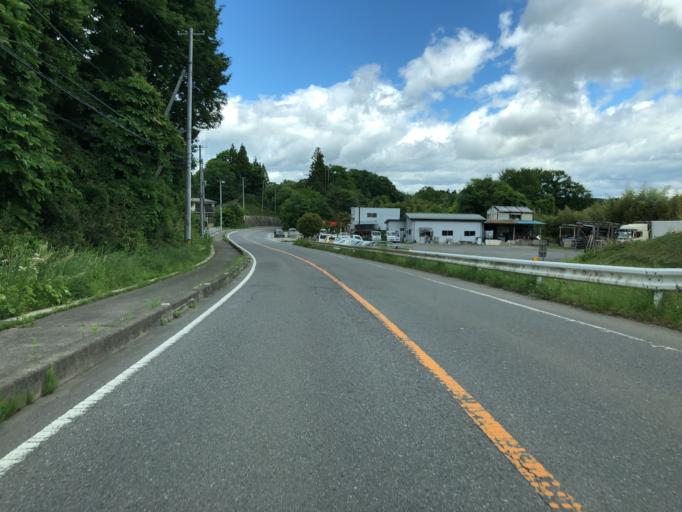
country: JP
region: Fukushima
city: Nihommatsu
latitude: 37.5749
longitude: 140.4562
